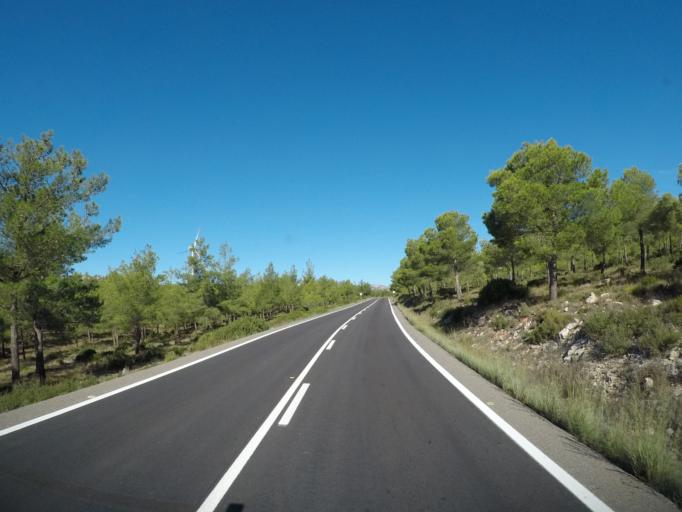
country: ES
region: Catalonia
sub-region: Provincia de Tarragona
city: El Perello
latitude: 40.8932
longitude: 0.6768
